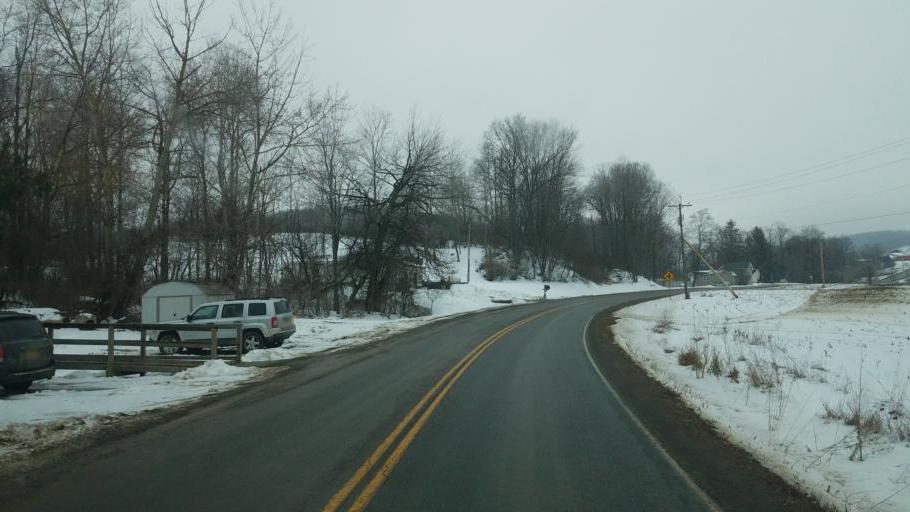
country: US
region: Pennsylvania
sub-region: Tioga County
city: Westfield
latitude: 42.0203
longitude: -77.5692
